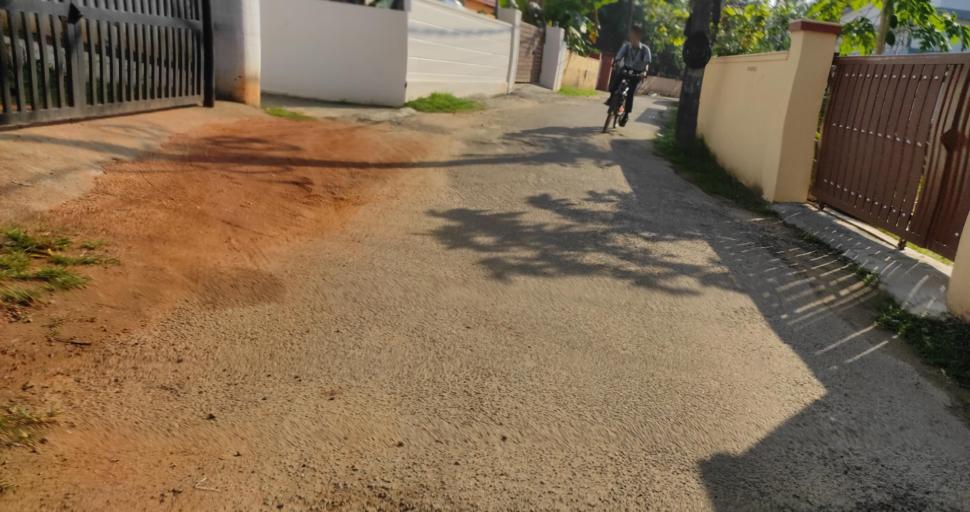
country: IN
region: Kerala
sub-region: Kottayam
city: Kottayam
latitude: 9.5804
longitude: 76.5019
